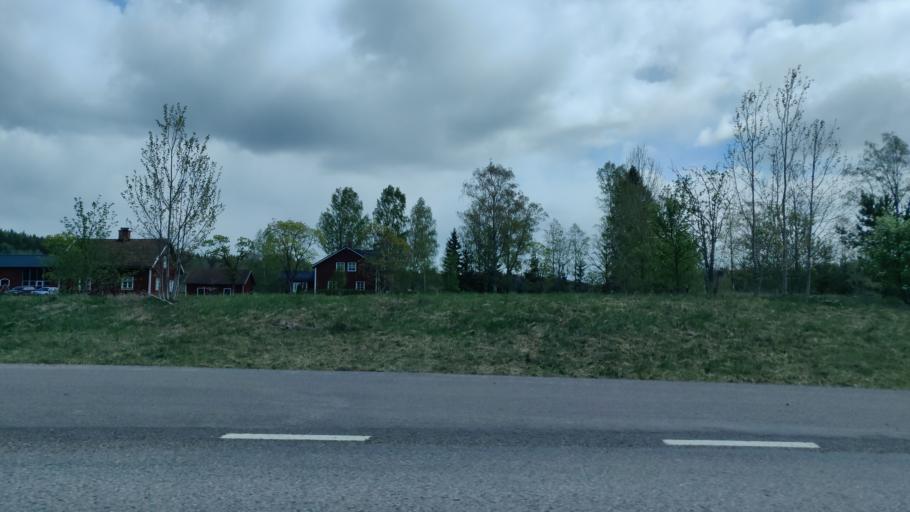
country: SE
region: Vaermland
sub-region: Karlstads Kommun
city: Molkom
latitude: 59.6233
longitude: 13.7305
